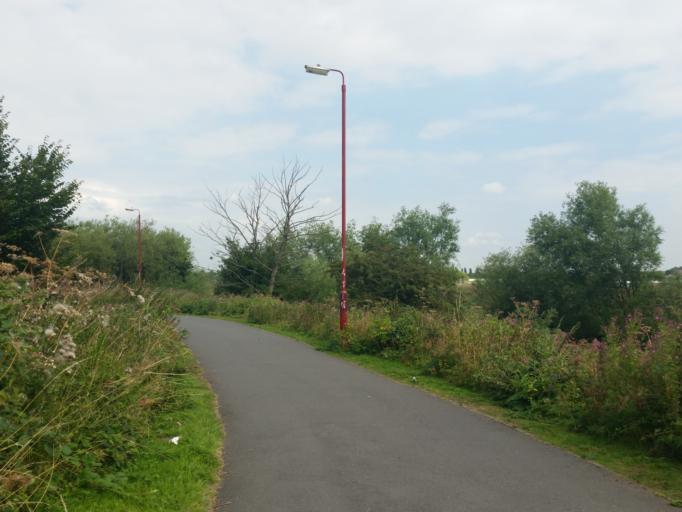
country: GB
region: England
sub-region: Derby
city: Derby
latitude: 52.9132
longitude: -1.4411
